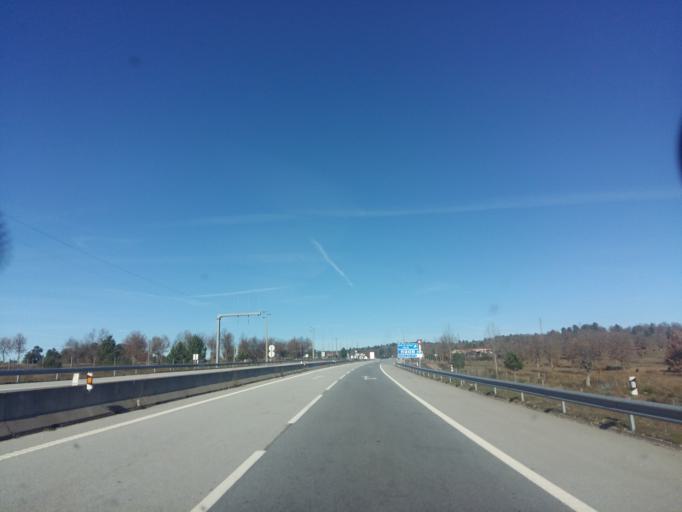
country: PT
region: Guarda
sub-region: Guarda
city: Sequeira
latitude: 40.5394
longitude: -7.2172
